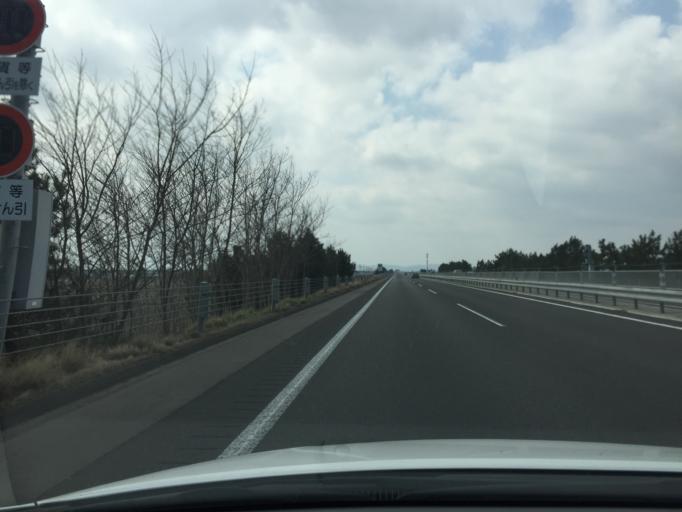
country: JP
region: Miyagi
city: Iwanuma
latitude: 38.1700
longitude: 140.9182
